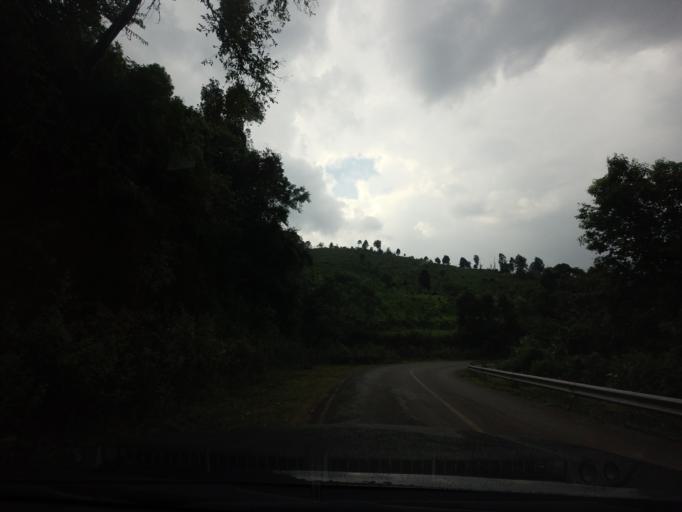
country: TH
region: Nan
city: Bo Kluea
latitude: 19.3467
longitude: 101.1589
